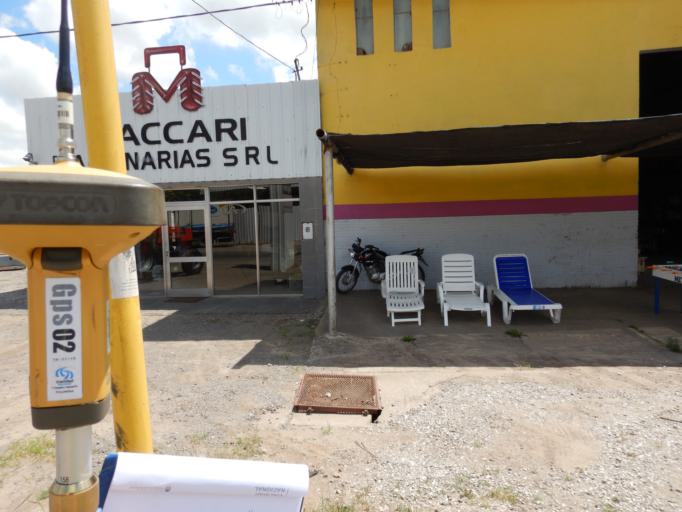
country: AR
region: Santa Fe
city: Canada de Gomez
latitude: -32.8075
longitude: -61.4106
